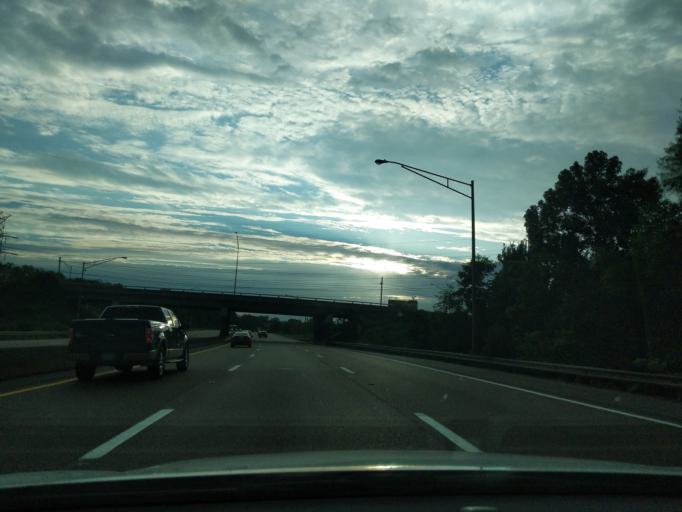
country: US
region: Tennessee
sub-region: Shelby County
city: New South Memphis
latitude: 35.0803
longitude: -90.0618
